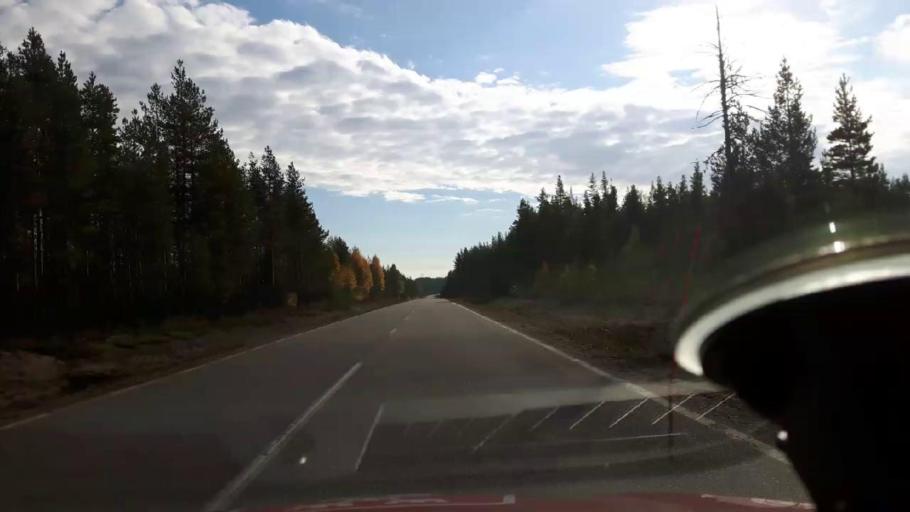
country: SE
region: Vaesternorrland
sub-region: Ange Kommun
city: Ange
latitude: 62.0577
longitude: 15.1230
